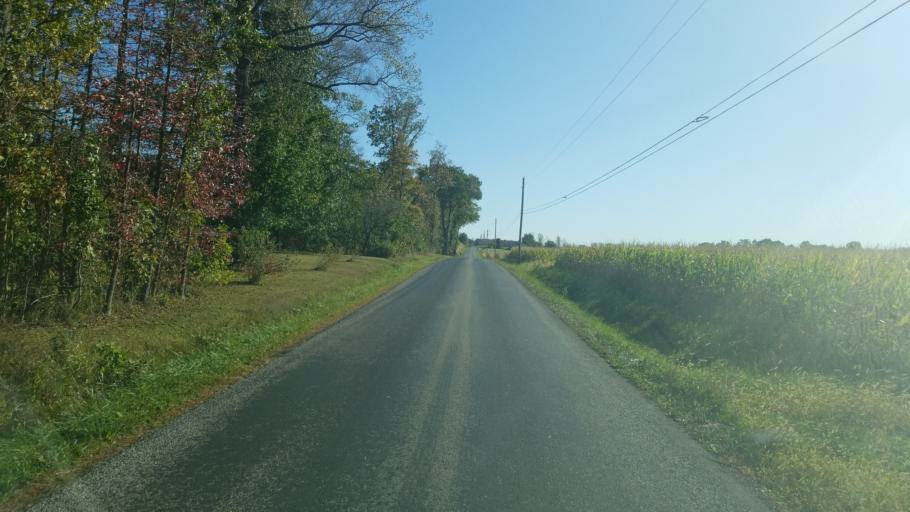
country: US
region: Ohio
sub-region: Wayne County
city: Creston
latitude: 40.9441
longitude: -81.9759
